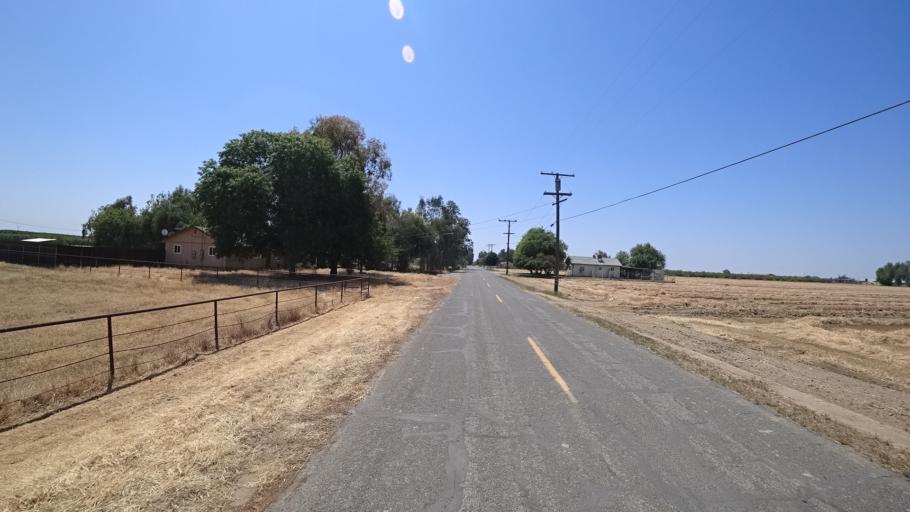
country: US
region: California
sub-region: Kings County
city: Armona
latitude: 36.2966
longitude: -119.6912
